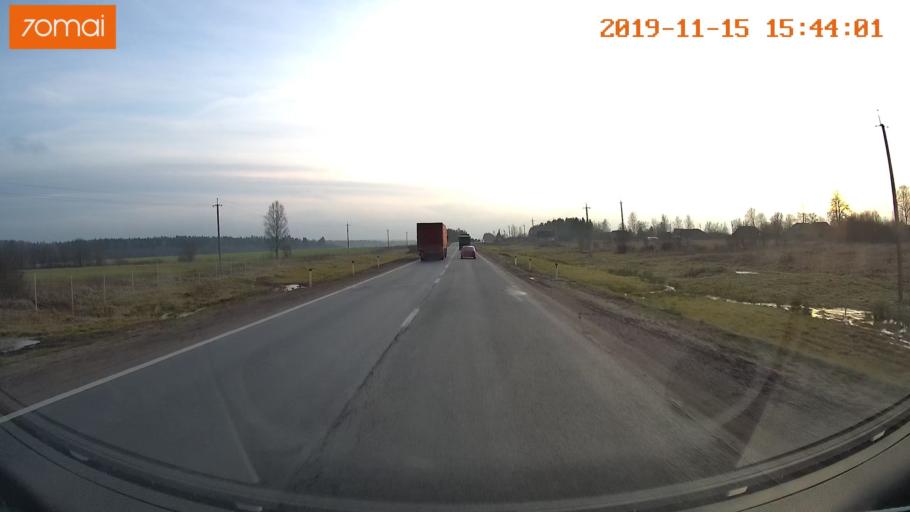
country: RU
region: Jaroslavl
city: Danilov
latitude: 57.9752
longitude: 40.0245
